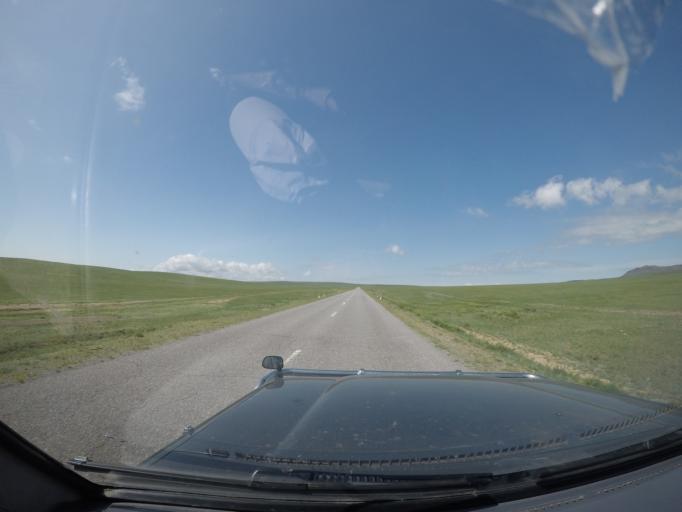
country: MN
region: Hentiy
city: Bayan
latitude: 47.3165
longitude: 111.3591
